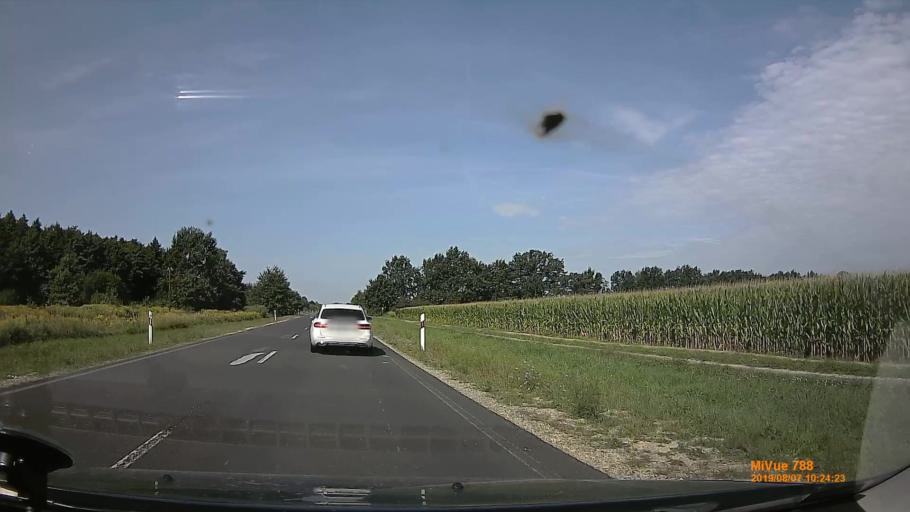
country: HU
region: Zala
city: Lenti
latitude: 46.6216
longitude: 16.5135
